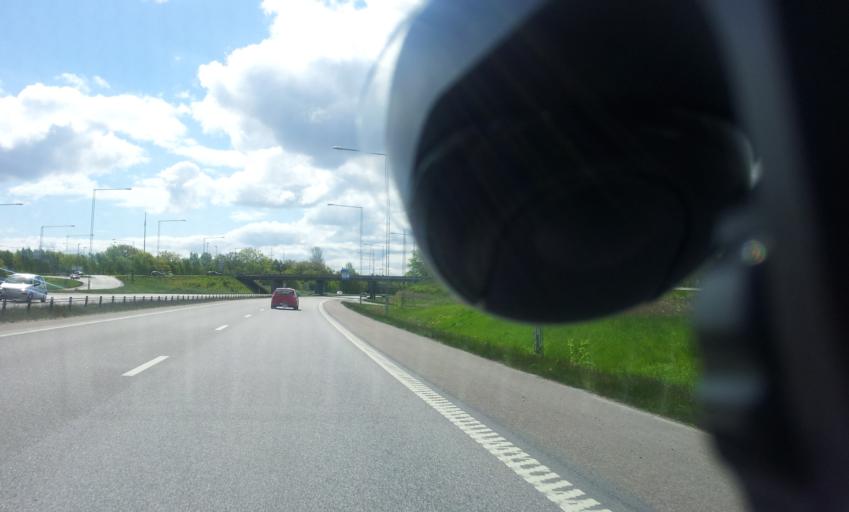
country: SE
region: Kalmar
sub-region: Kalmar Kommun
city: Kalmar
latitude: 56.6854
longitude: 16.3253
